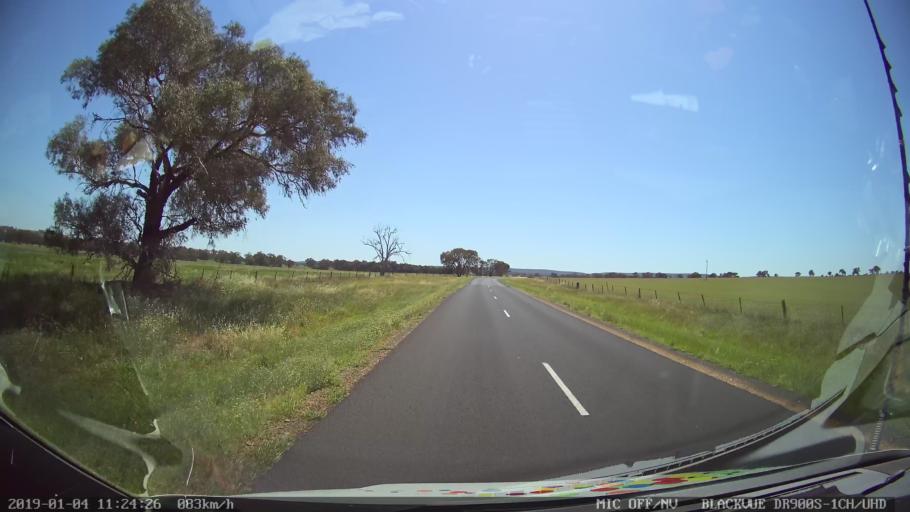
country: AU
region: New South Wales
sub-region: Cabonne
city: Molong
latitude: -33.1325
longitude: 148.7469
